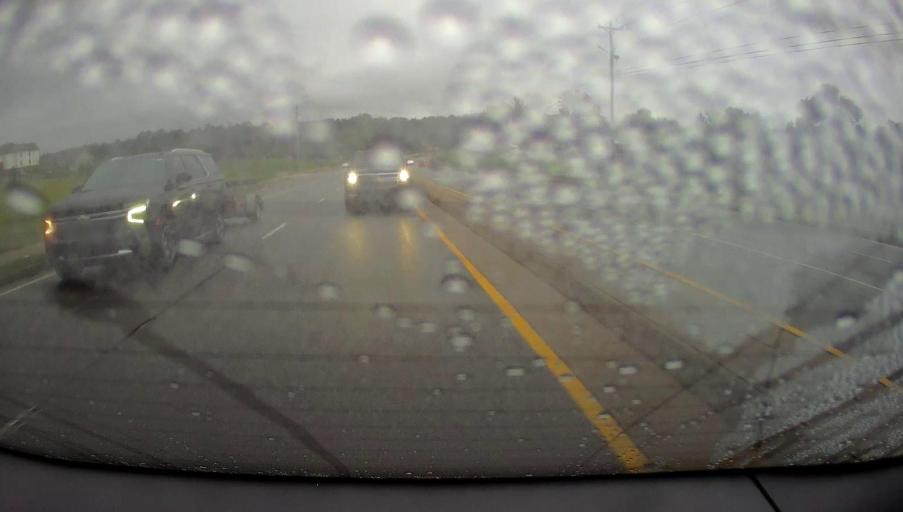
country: US
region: Georgia
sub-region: Houston County
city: Centerville
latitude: 32.5727
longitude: -83.6626
